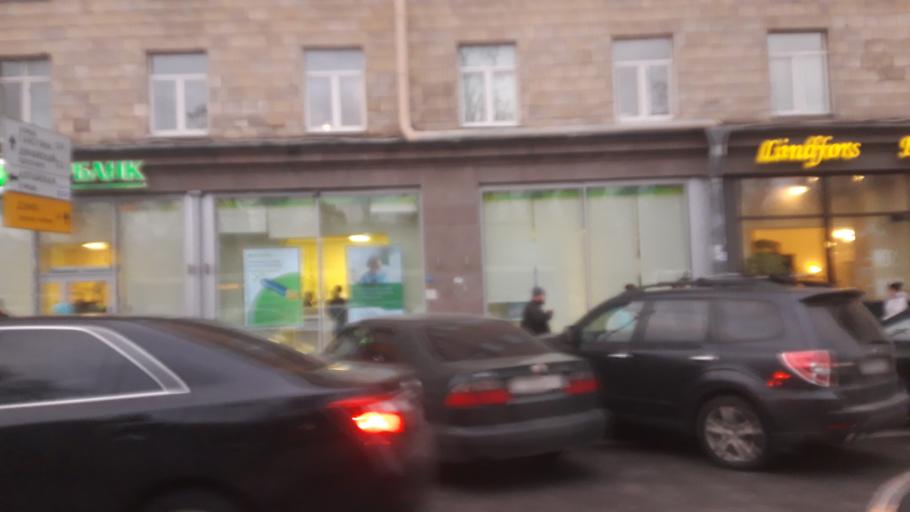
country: RU
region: St.-Petersburg
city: Kupchino
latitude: 59.8501
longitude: 30.3212
